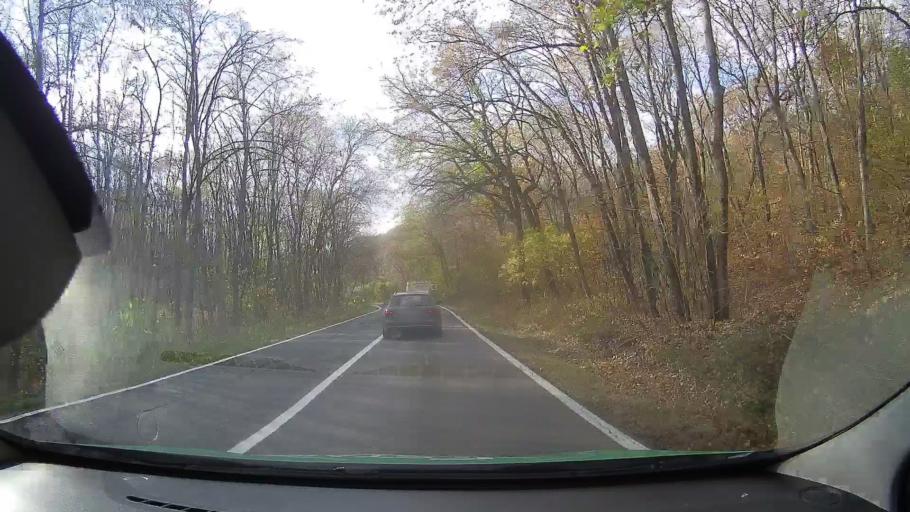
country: RO
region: Tulcea
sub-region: Comuna Ciucurova
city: Ciucurova
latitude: 44.9241
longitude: 28.4351
